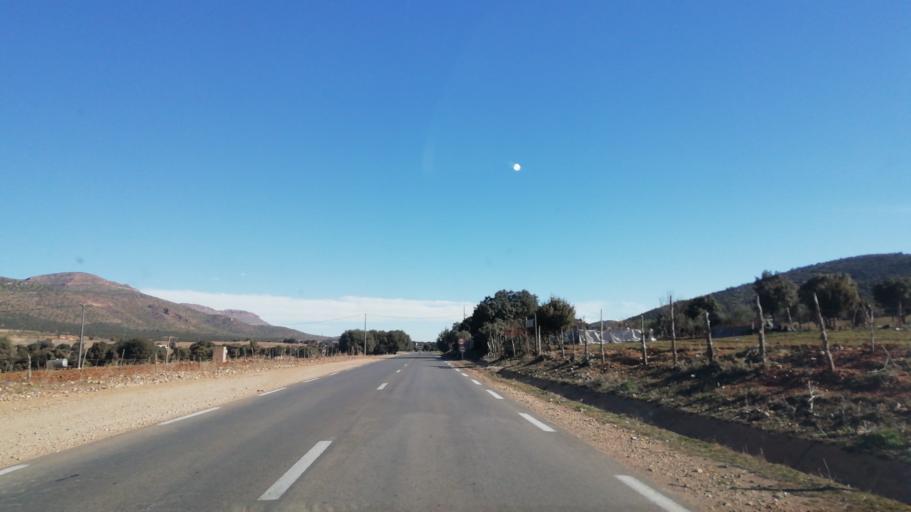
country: DZ
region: Tlemcen
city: Sebdou
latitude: 34.6913
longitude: -1.2416
